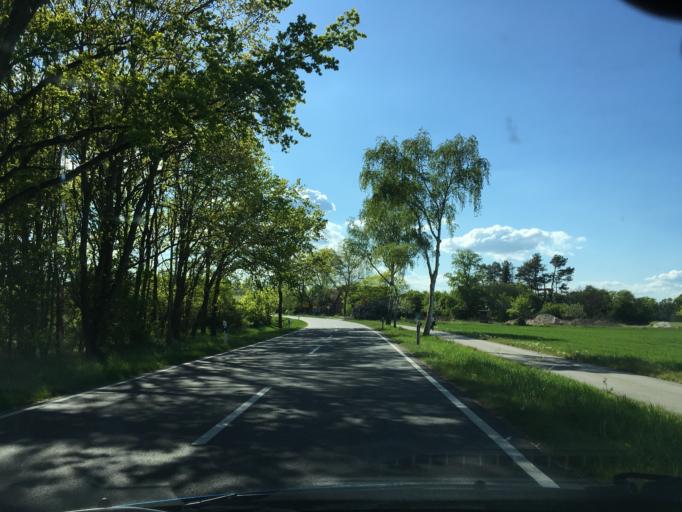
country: DE
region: Lower Saxony
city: Gartow
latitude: 53.0271
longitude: 11.4778
